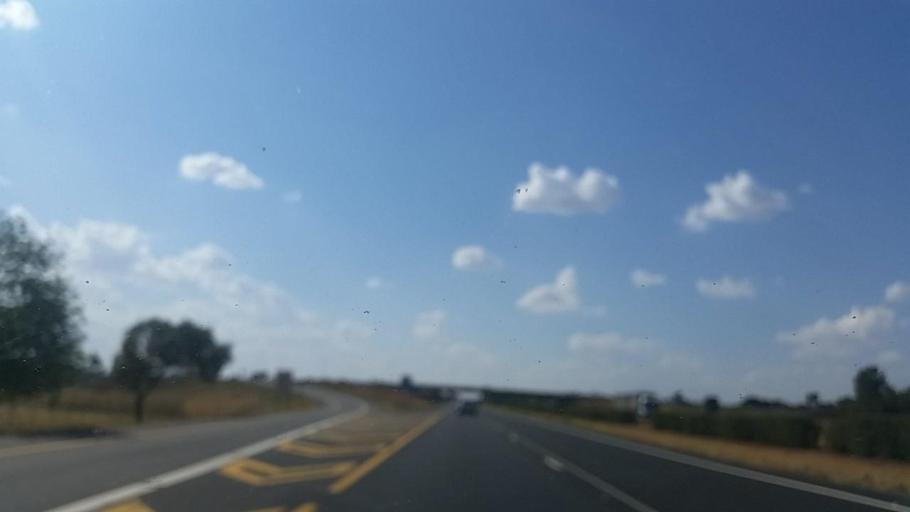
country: ZA
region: Orange Free State
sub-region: Mangaung Metropolitan Municipality
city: Bloemfontein
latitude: -29.1685
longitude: 26.1830
